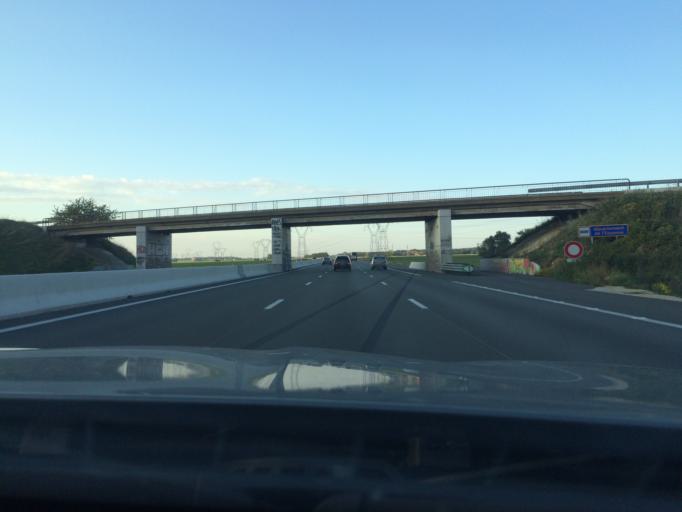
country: FR
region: Ile-de-France
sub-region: Departement de l'Essonne
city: Le Coudray-Montceaux
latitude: 48.5275
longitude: 2.5024
